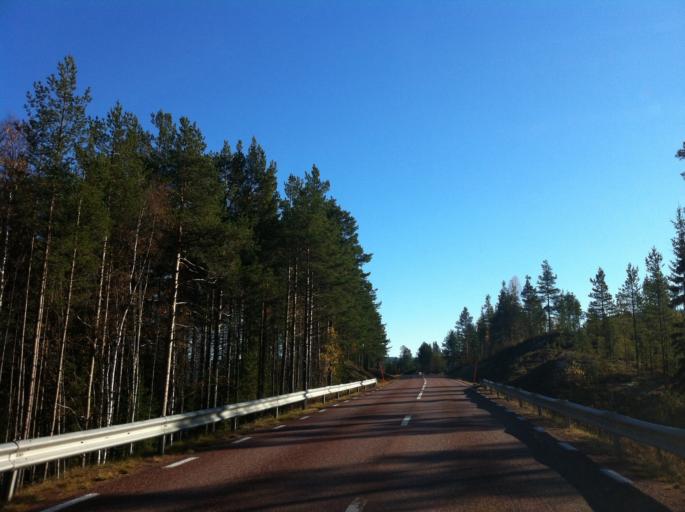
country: SE
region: Dalarna
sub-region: Alvdalens Kommun
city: AElvdalen
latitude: 61.3004
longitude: 13.7283
